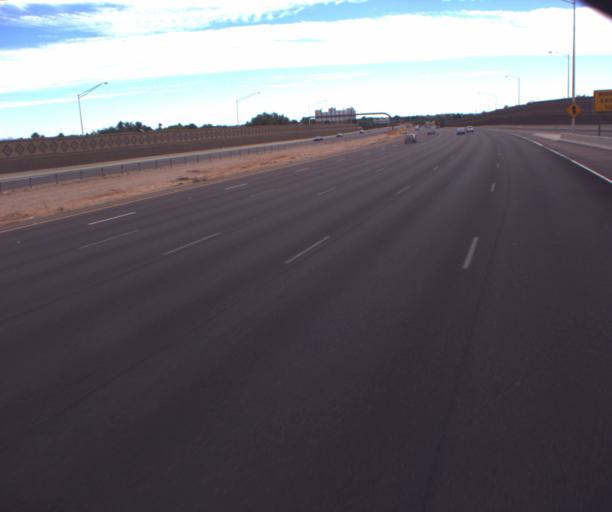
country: US
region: Arizona
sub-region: Pinal County
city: Apache Junction
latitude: 33.3756
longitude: -111.6485
